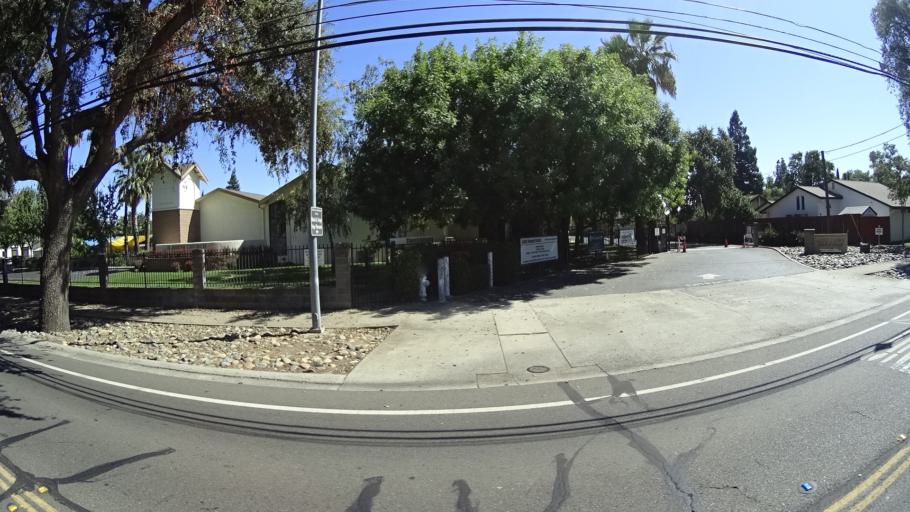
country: US
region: California
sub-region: Sacramento County
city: Elk Grove
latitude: 38.3957
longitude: -121.3715
